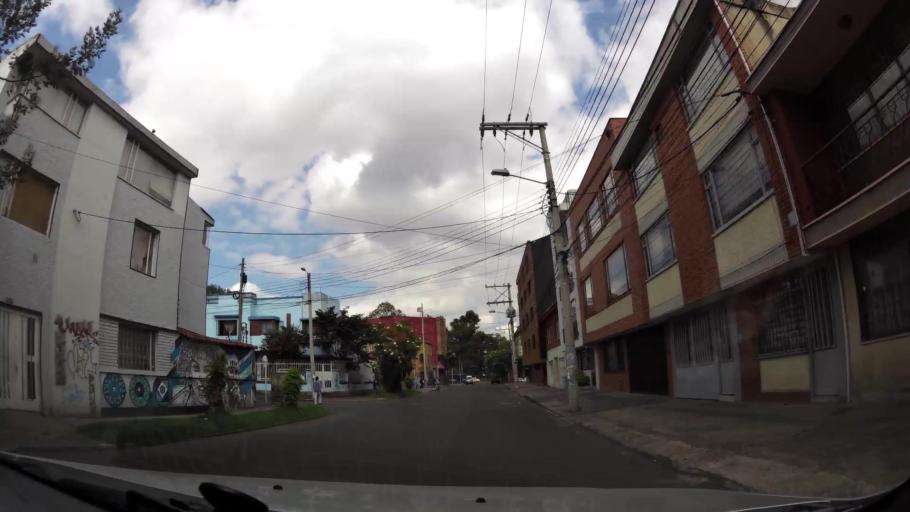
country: CO
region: Bogota D.C.
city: Bogota
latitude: 4.6315
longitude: -74.0710
